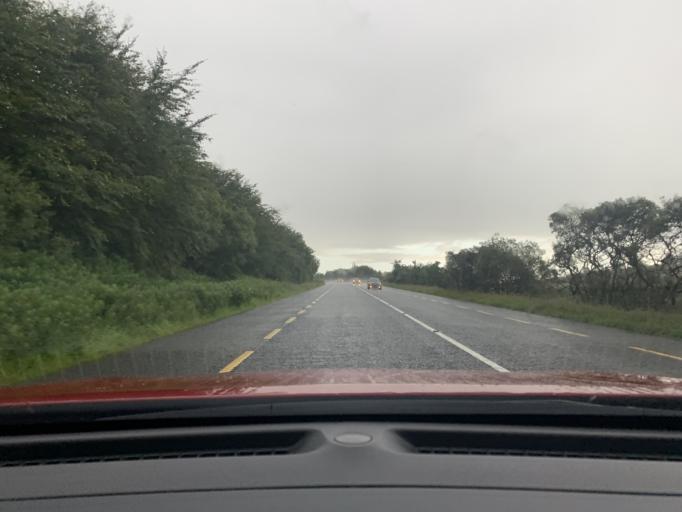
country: IE
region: Ulster
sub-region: County Donegal
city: Letterkenny
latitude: 54.8959
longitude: -7.7279
